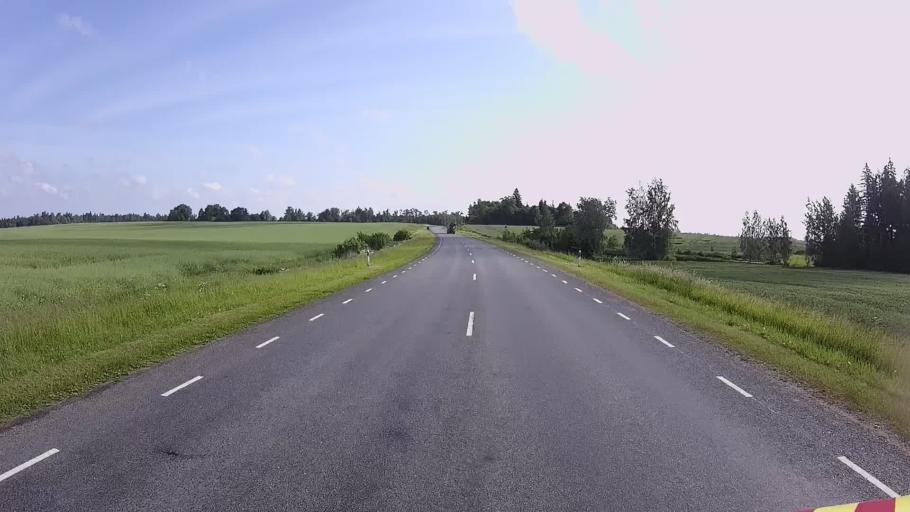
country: EE
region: Viljandimaa
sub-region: Viiratsi vald
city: Viiratsi
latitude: 58.3333
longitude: 25.6154
